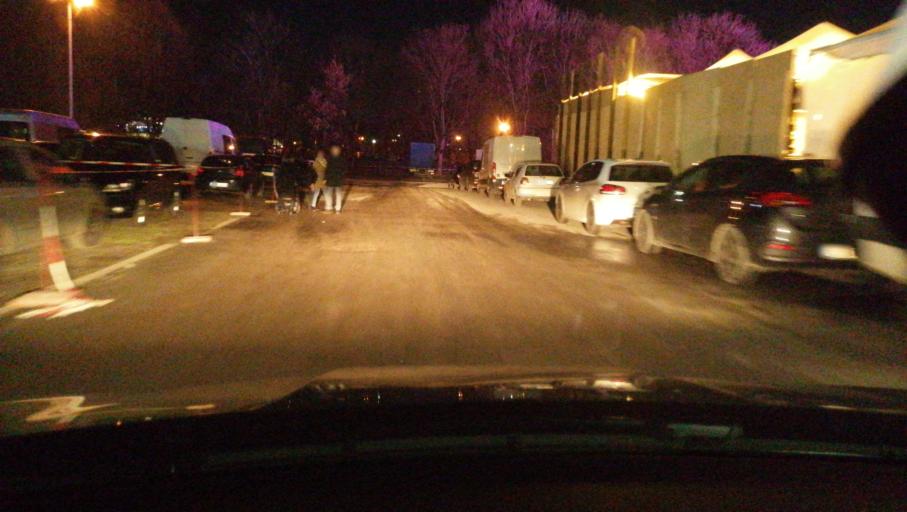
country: DE
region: North Rhine-Westphalia
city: Bochum-Hordel
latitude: 51.5458
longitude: 7.1575
